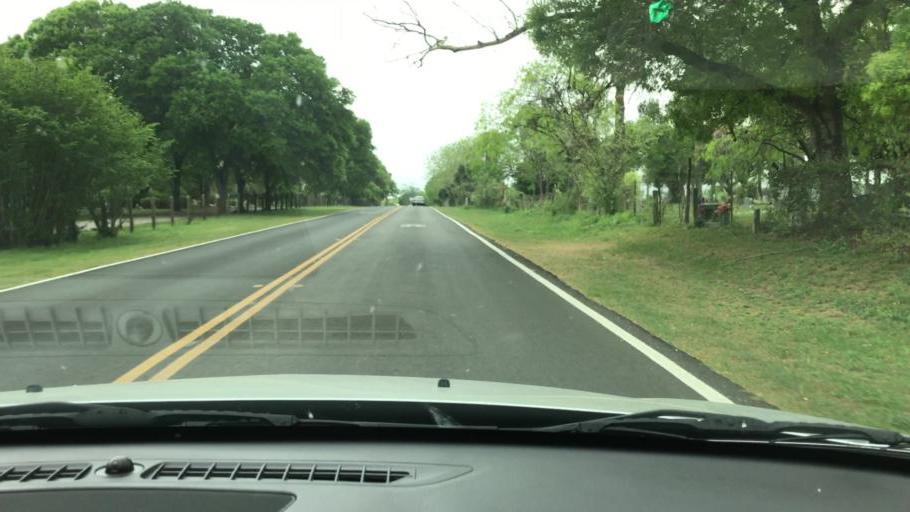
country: US
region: Texas
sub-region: Bexar County
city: San Antonio
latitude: 29.3452
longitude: -98.4717
